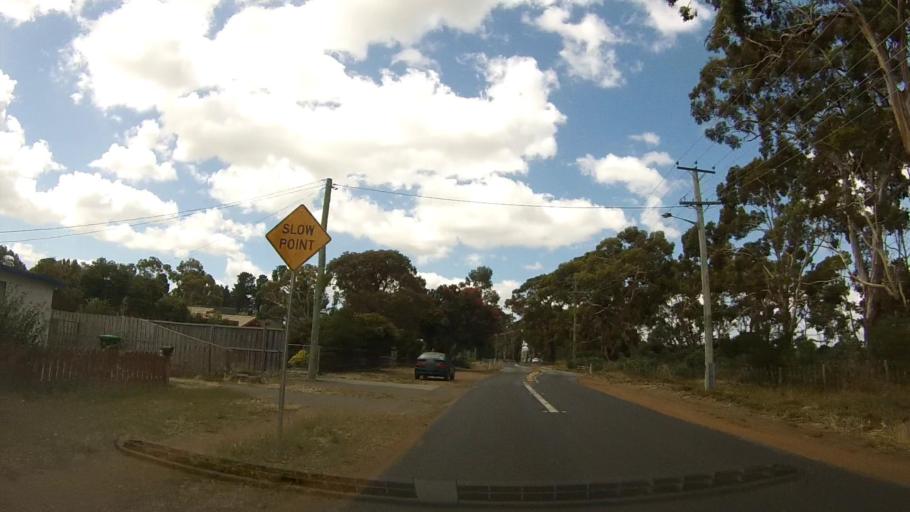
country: AU
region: Tasmania
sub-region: Clarence
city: Seven Mile Beach
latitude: -42.8565
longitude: 147.5105
